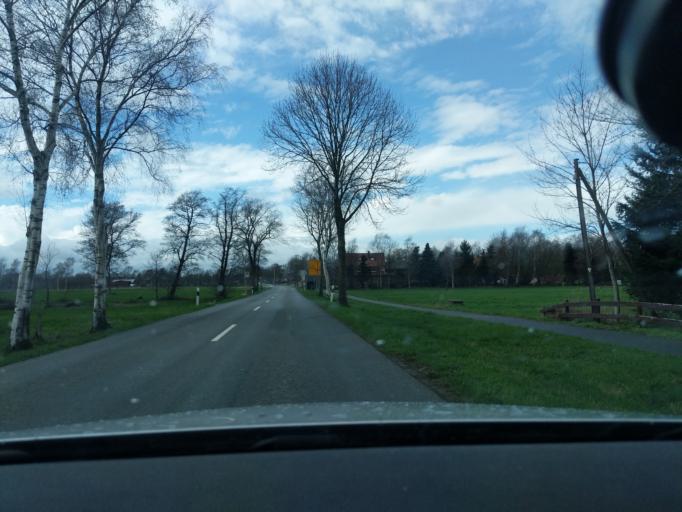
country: DE
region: Lower Saxony
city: Drochtersen
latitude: 53.6677
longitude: 9.3867
